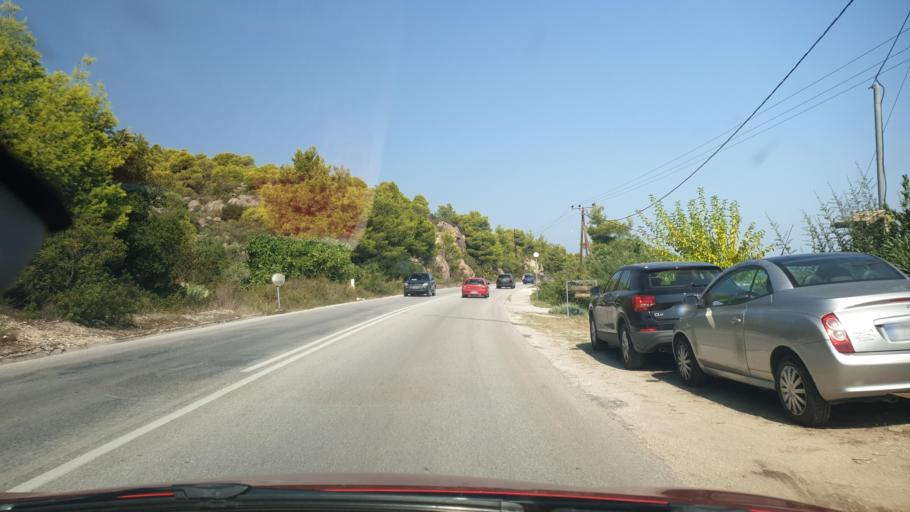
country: GR
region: Central Macedonia
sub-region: Nomos Chalkidikis
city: Agios Nikolaos
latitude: 40.2291
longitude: 23.7375
